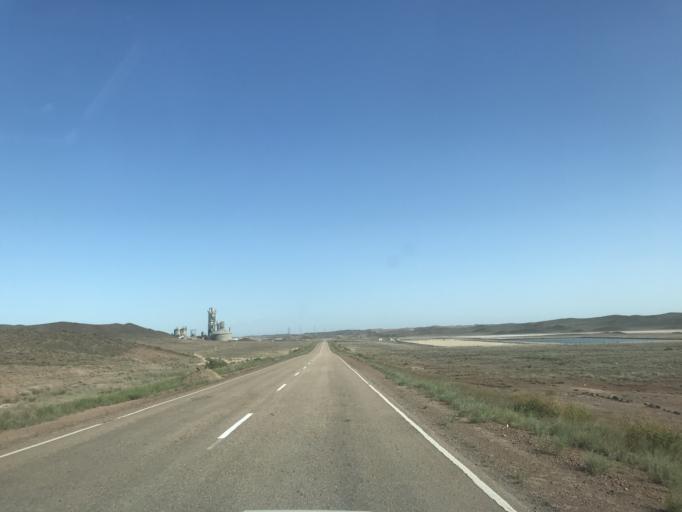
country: KZ
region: Zhambyl
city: Mynaral
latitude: 45.4002
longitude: 73.6386
